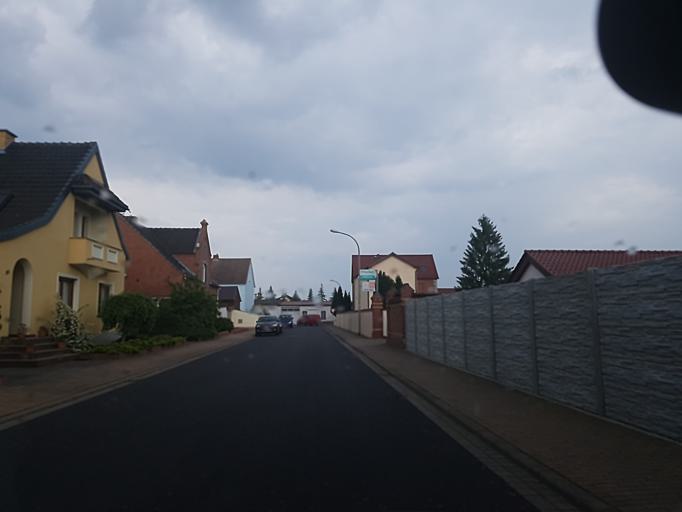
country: DE
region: Saxony-Anhalt
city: Elster
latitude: 51.8300
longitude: 12.8280
